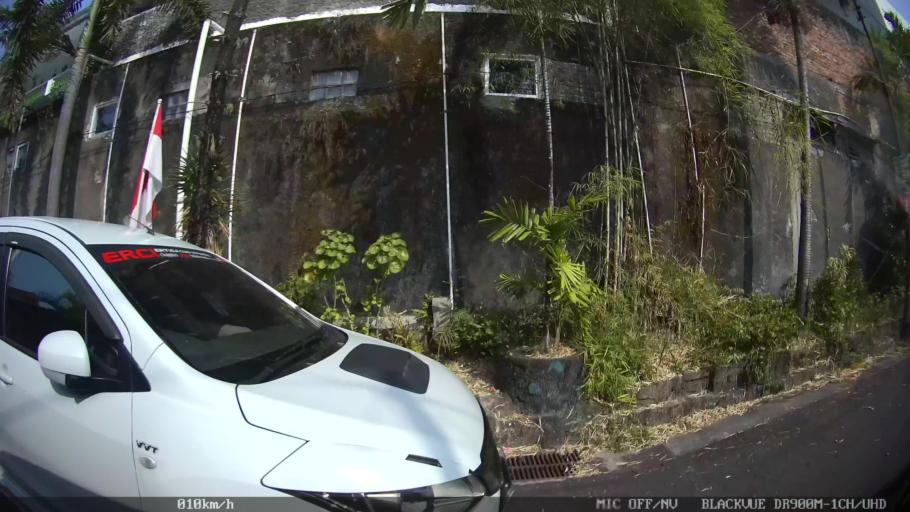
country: ID
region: Daerah Istimewa Yogyakarta
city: Yogyakarta
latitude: -7.8144
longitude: 110.3702
